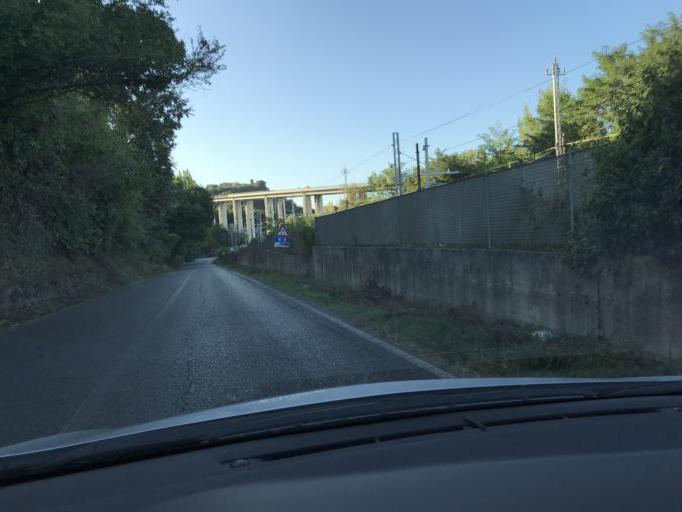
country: IT
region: Latium
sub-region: Provincia di Viterbo
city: Orte
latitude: 42.4484
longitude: 12.3913
